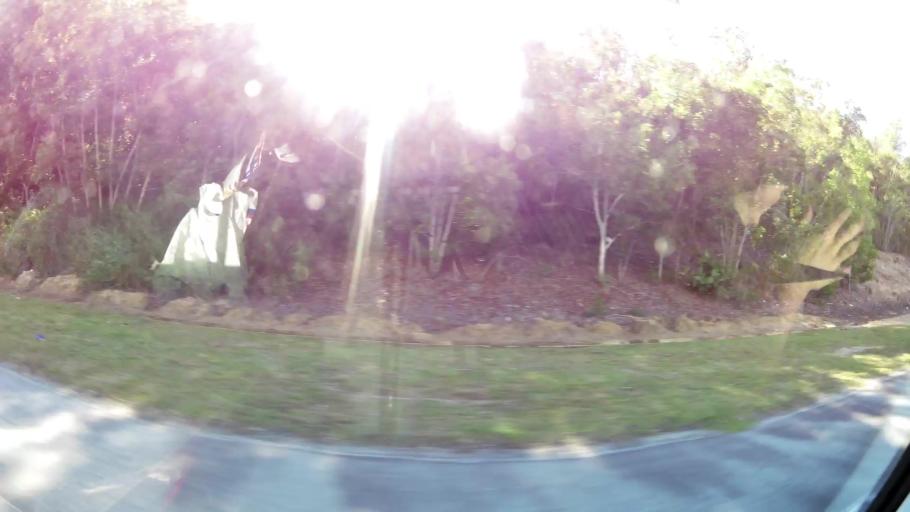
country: BN
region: Brunei and Muara
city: Bandar Seri Begawan
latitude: 4.9805
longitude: 114.9333
